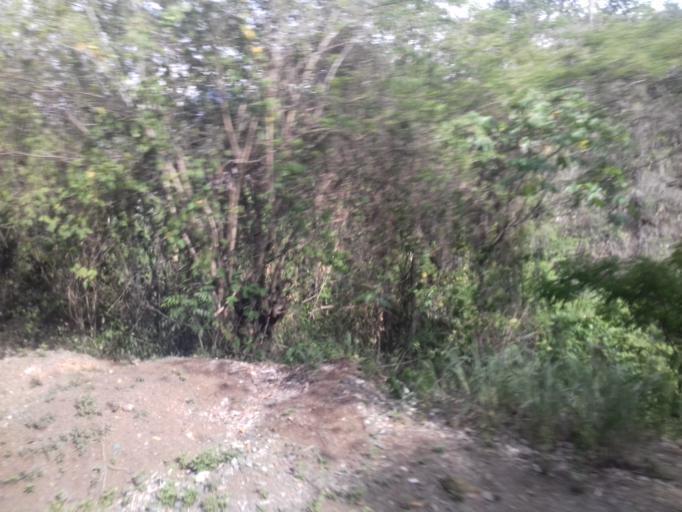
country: CO
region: Antioquia
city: Venecia
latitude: 5.9706
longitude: -75.8272
